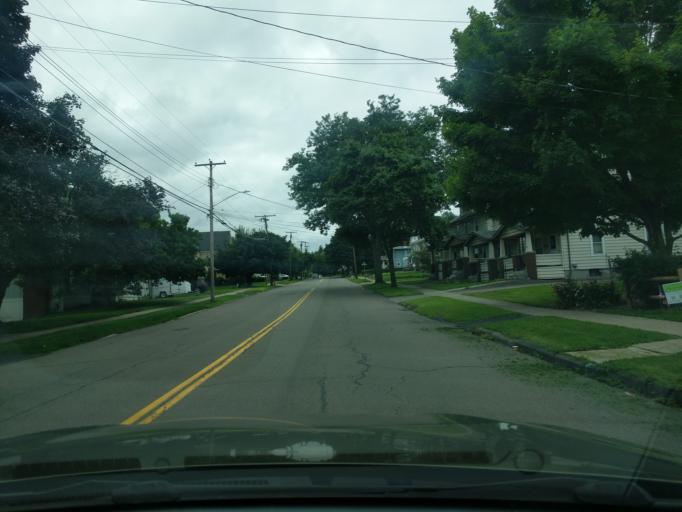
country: US
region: New York
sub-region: Chemung County
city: Elmira
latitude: 42.1047
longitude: -76.8183
